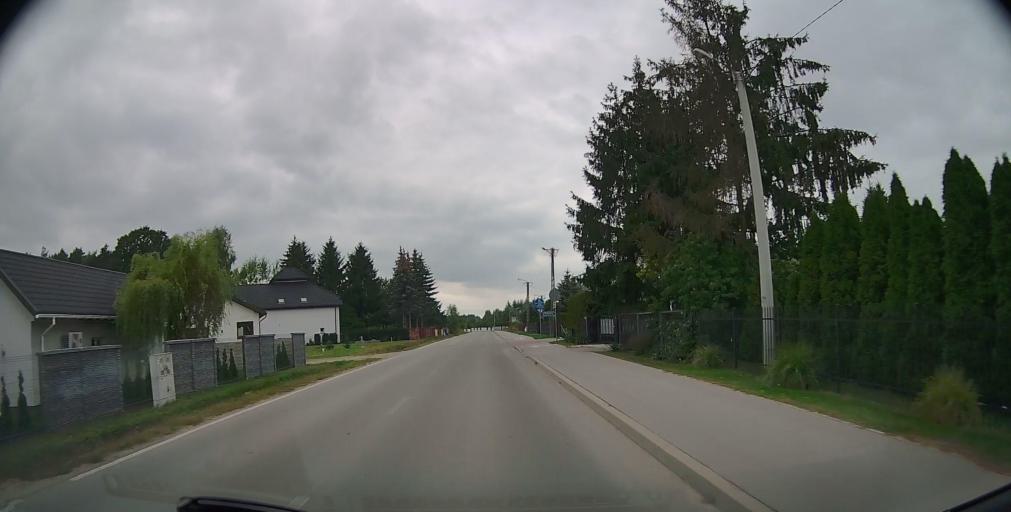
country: PL
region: Masovian Voivodeship
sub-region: Powiat radomski
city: Zakrzew
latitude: 51.4308
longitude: 21.0564
